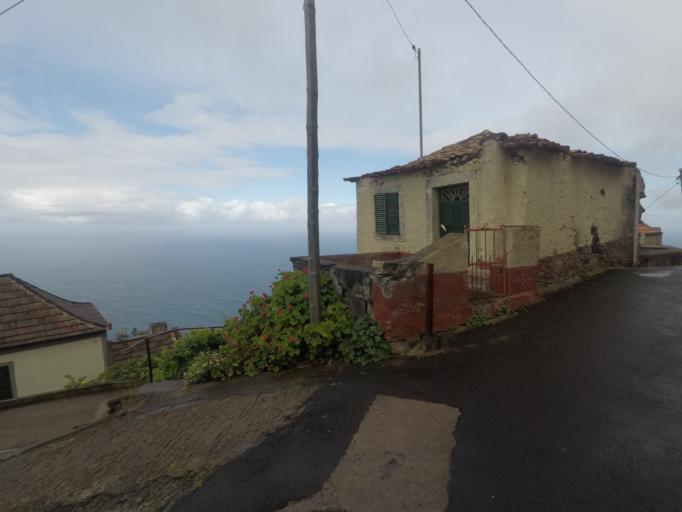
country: PT
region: Madeira
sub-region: Calheta
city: Faja da Ovelha
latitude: 32.7756
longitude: -17.2363
